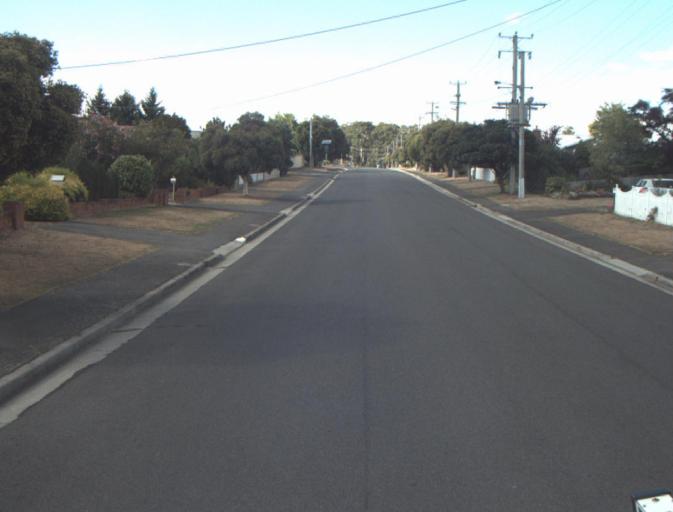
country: AU
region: Tasmania
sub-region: Launceston
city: Newstead
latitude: -41.4605
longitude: 147.1722
